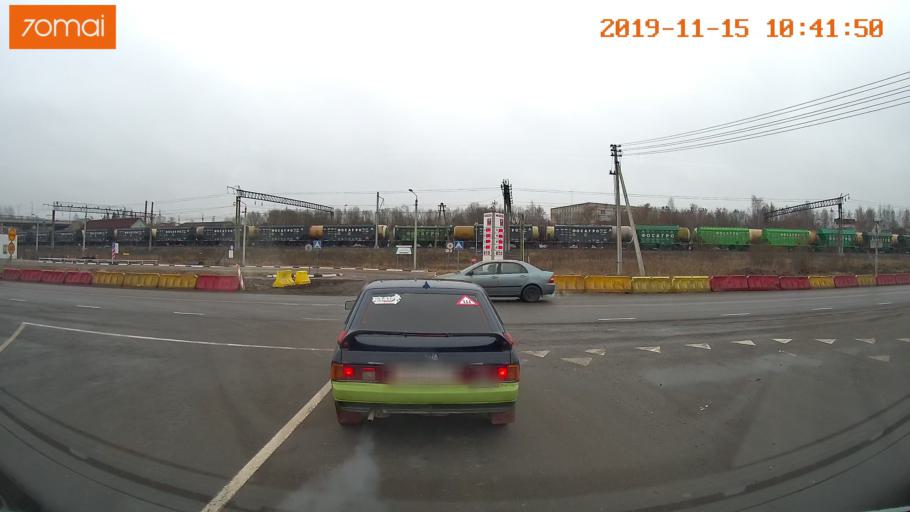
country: RU
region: Vologda
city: Sheksna
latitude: 59.2105
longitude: 38.5127
